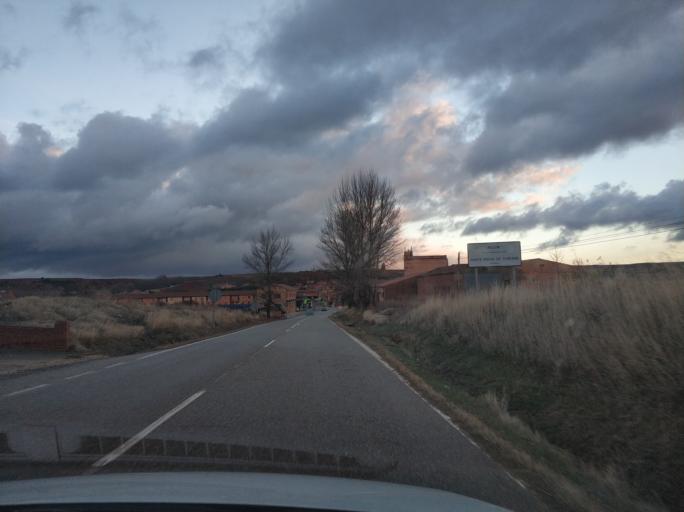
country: ES
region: Castille and Leon
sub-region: Provincia de Segovia
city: Ayllon
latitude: 41.4171
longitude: -3.3852
